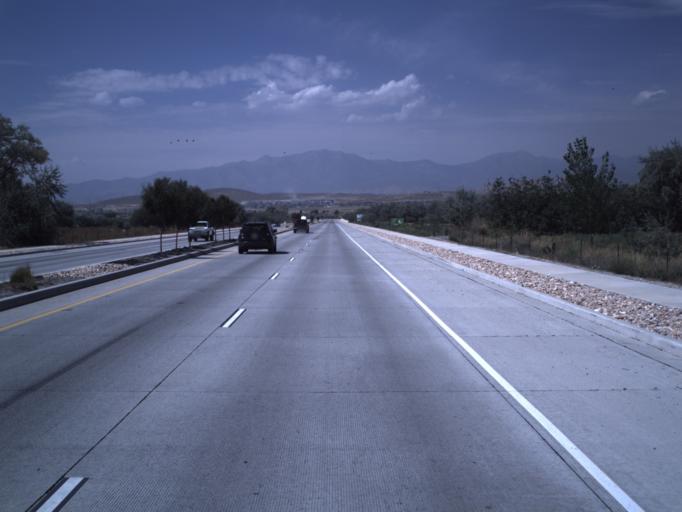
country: US
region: Utah
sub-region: Utah County
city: Saratoga Springs
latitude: 40.3763
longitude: -111.8913
